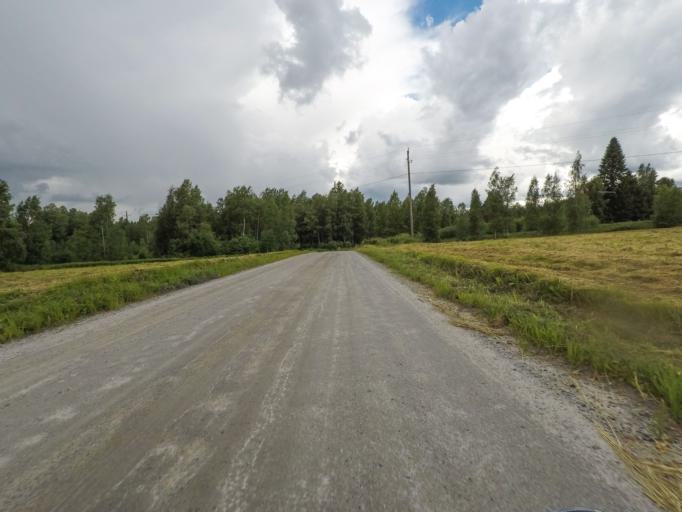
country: FI
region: Central Finland
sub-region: Jyvaeskylae
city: Hankasalmi
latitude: 62.4169
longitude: 26.6242
